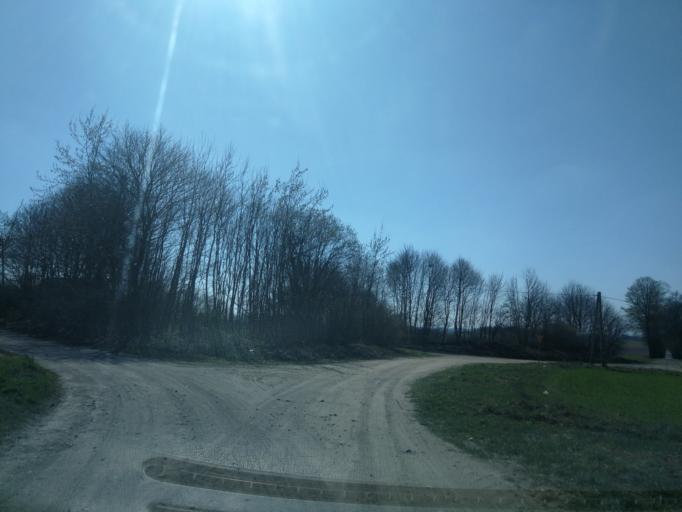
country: PL
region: Warmian-Masurian Voivodeship
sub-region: Powiat ostrodzki
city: Dabrowno
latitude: 53.4385
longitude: 19.9803
